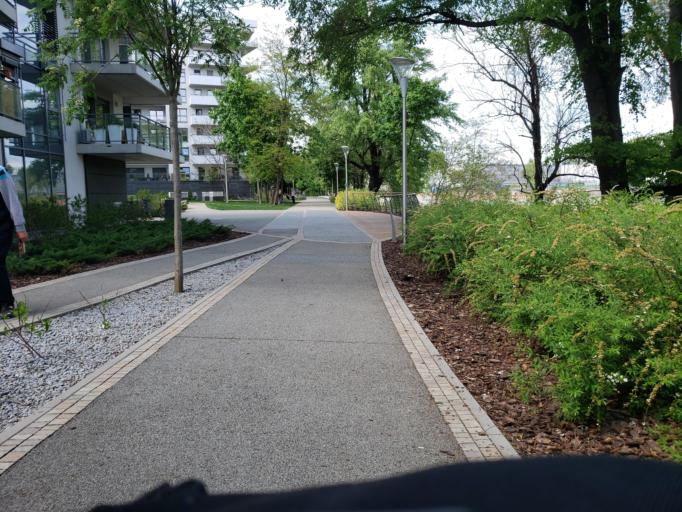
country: PL
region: Lower Silesian Voivodeship
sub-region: Powiat wroclawski
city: Wroclaw
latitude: 51.1188
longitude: 17.0252
